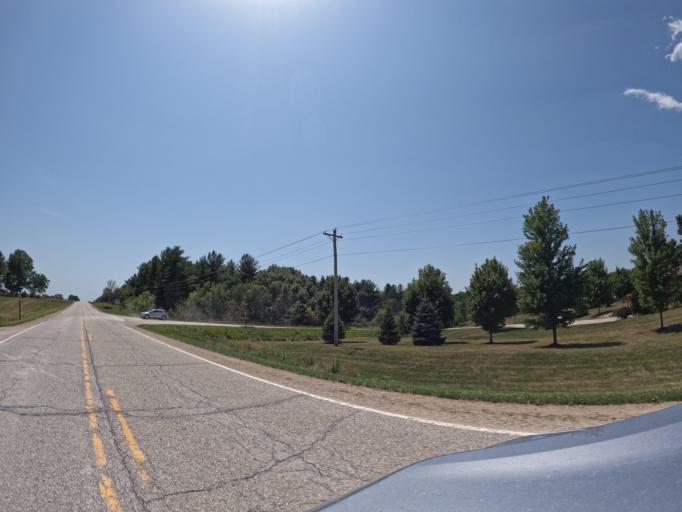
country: US
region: Iowa
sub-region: Henry County
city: Mount Pleasant
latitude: 40.9593
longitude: -91.6124
